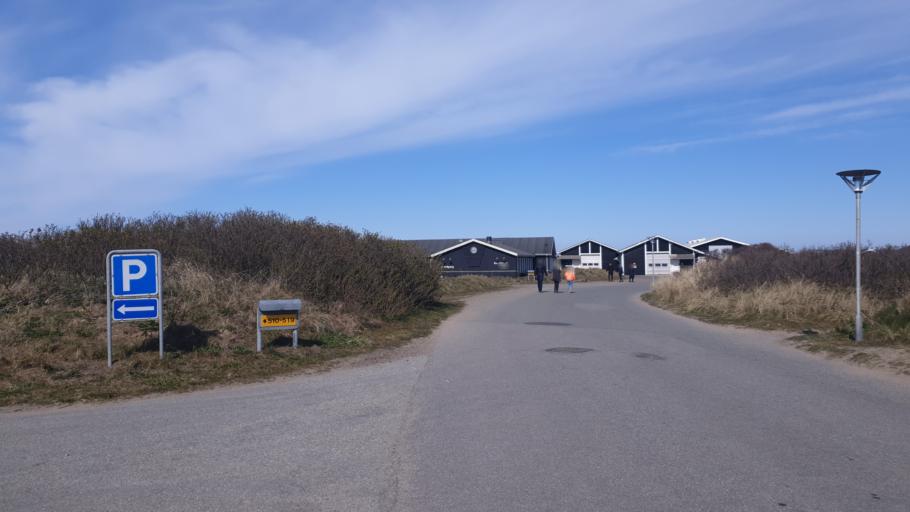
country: DK
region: North Denmark
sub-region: Hjorring Kommune
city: Hjorring
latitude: 57.4947
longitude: 9.8378
